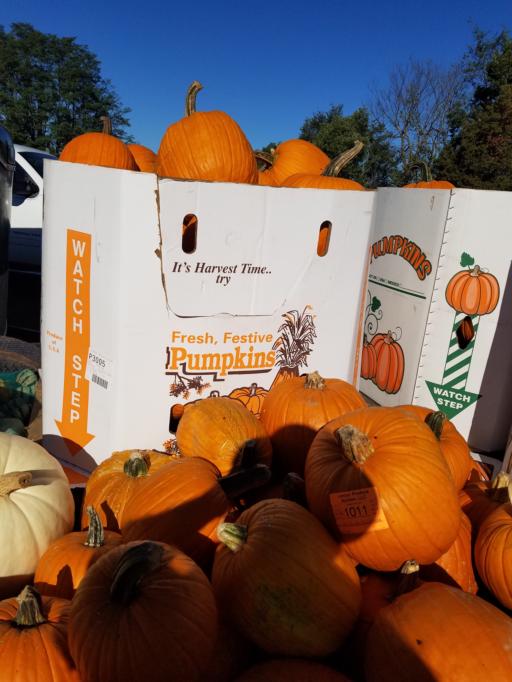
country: US
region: Iowa
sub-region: Decatur County
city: Lamoni
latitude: 40.6304
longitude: -93.8940
